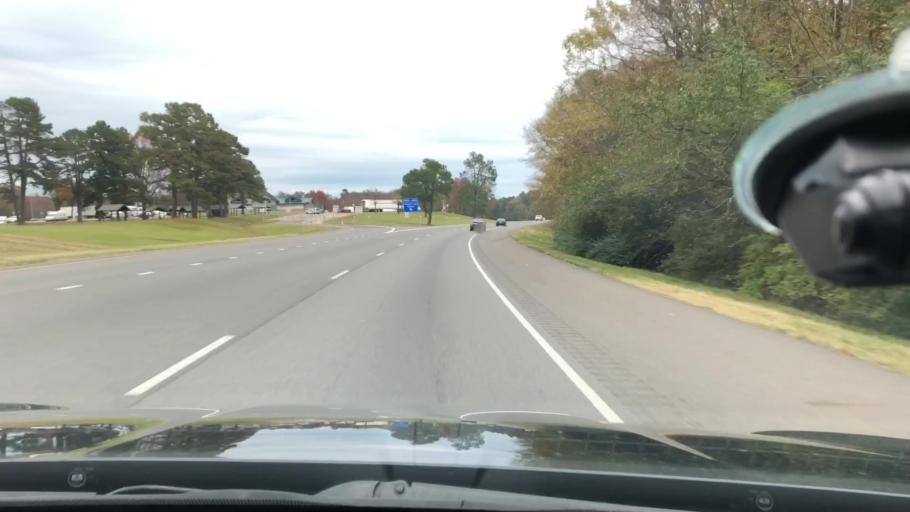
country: US
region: Arkansas
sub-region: Hot Spring County
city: Malvern
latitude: 34.3491
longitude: -92.8943
